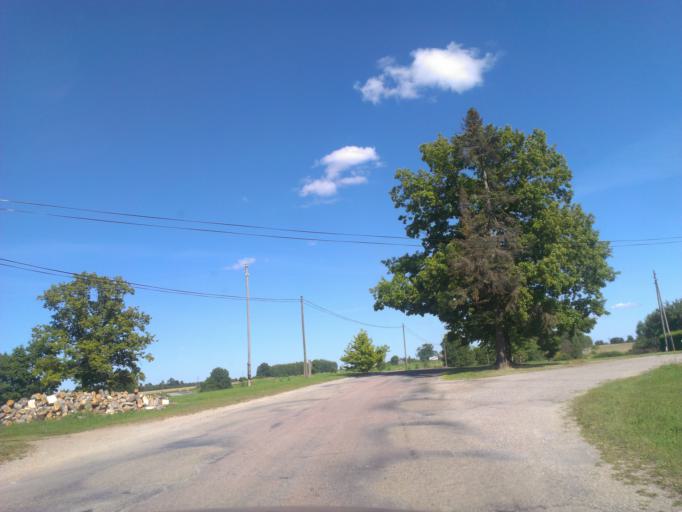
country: LV
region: Malpils
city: Malpils
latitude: 57.0134
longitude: 24.9734
